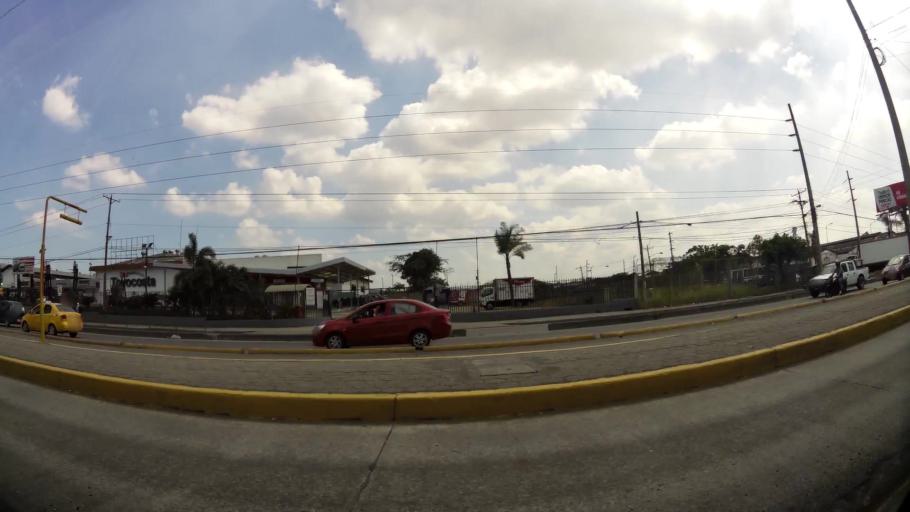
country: EC
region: Guayas
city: Guayaquil
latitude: -2.1168
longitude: -79.9324
